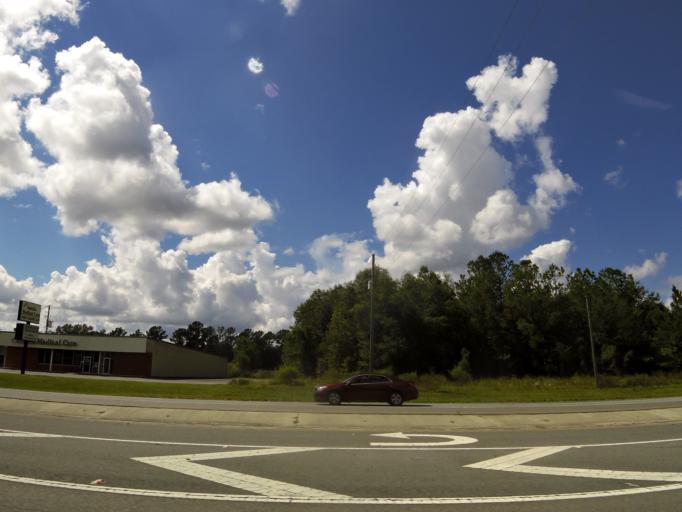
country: US
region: Georgia
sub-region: Charlton County
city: Folkston
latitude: 30.8220
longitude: -82.0027
